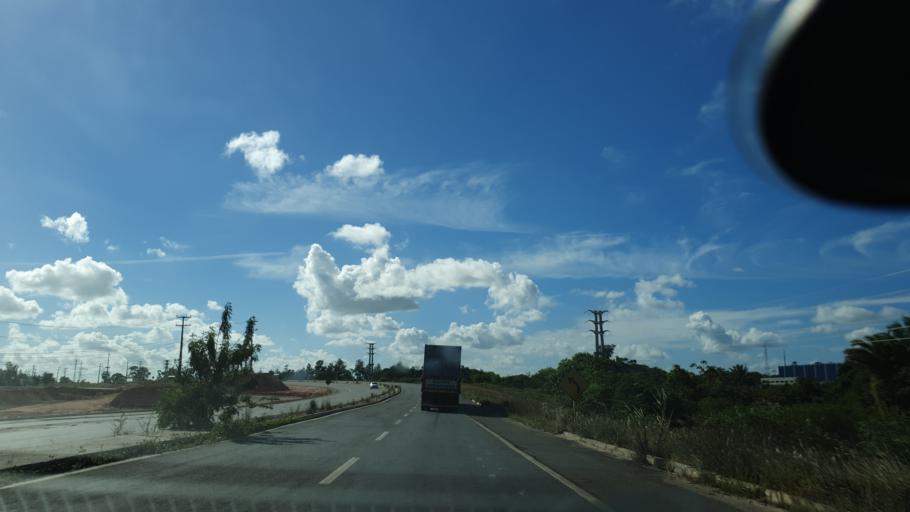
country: BR
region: Bahia
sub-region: Camacari
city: Camacari
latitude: -12.6839
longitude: -38.2638
